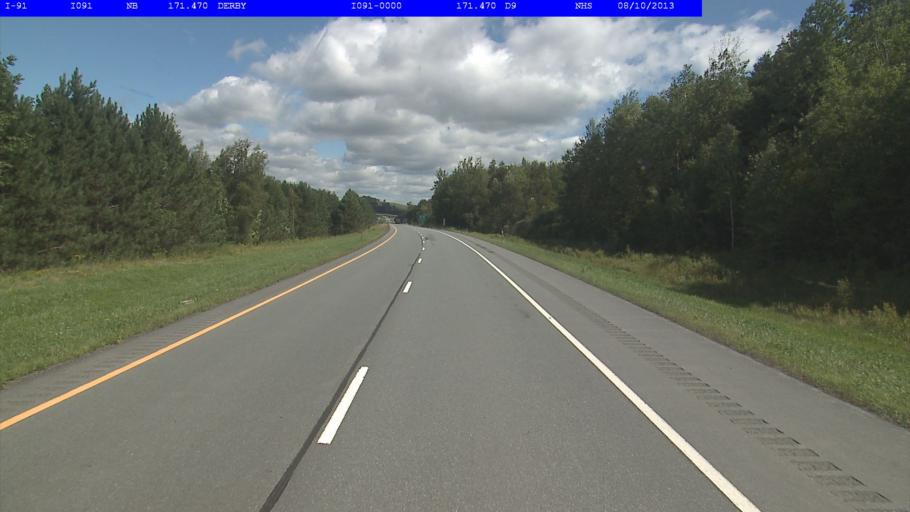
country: US
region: Vermont
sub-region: Orleans County
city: Newport
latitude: 44.9405
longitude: -72.1595
